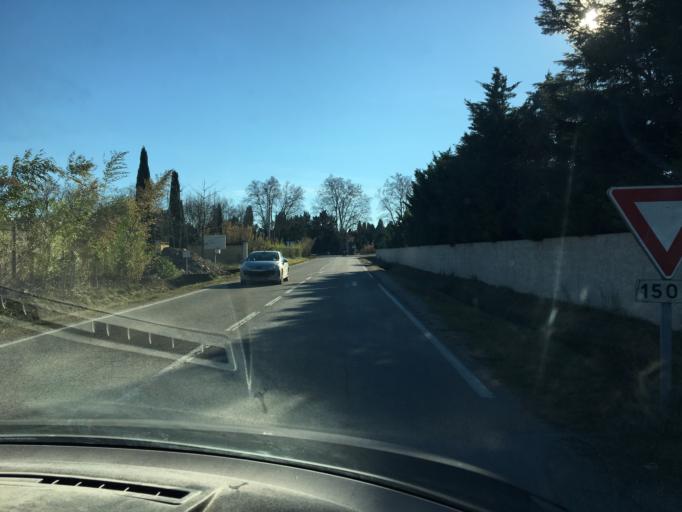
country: FR
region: Provence-Alpes-Cote d'Azur
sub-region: Departement des Bouches-du-Rhone
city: Maillane
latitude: 43.7972
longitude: 4.7888
